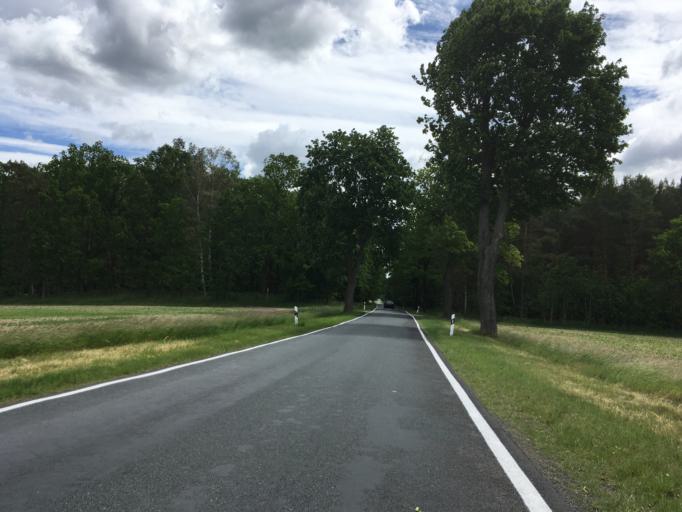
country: DE
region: Brandenburg
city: Melchow
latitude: 52.7379
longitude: 13.7381
